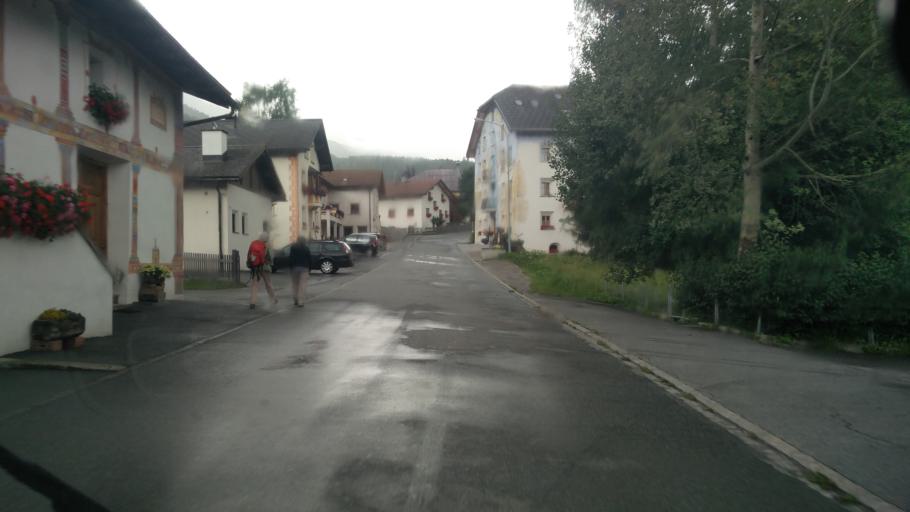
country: IT
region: Trentino-Alto Adige
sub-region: Bolzano
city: Tubre
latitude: 46.6002
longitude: 10.4079
